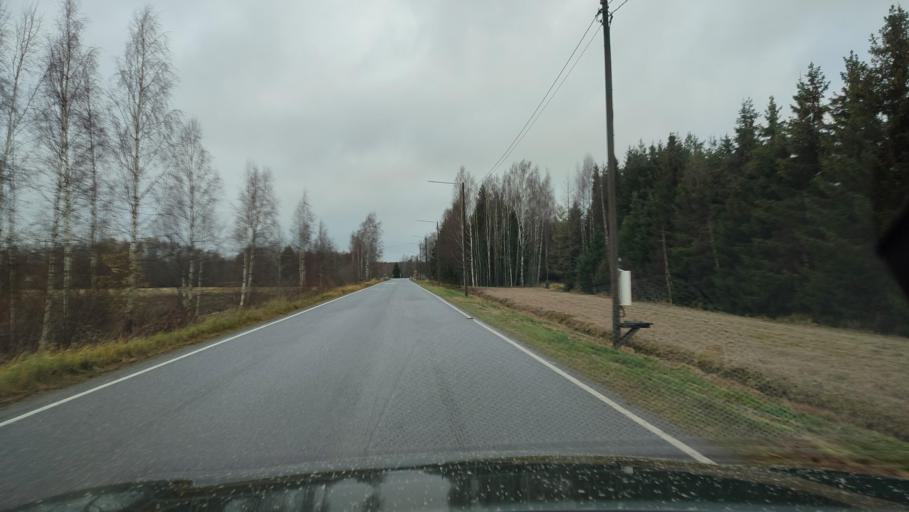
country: FI
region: Southern Ostrobothnia
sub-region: Suupohja
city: Teuva
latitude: 62.4580
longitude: 21.6052
